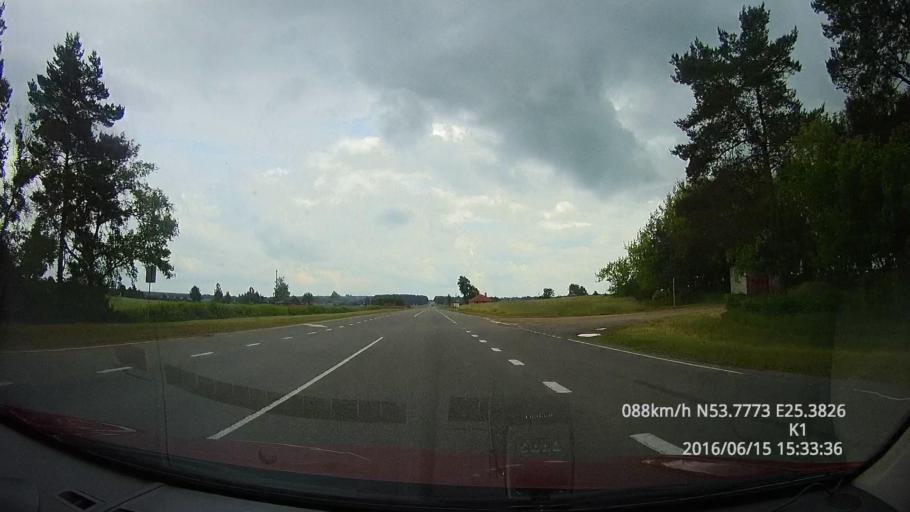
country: BY
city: Berezovka
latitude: 53.7766
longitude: 25.3830
